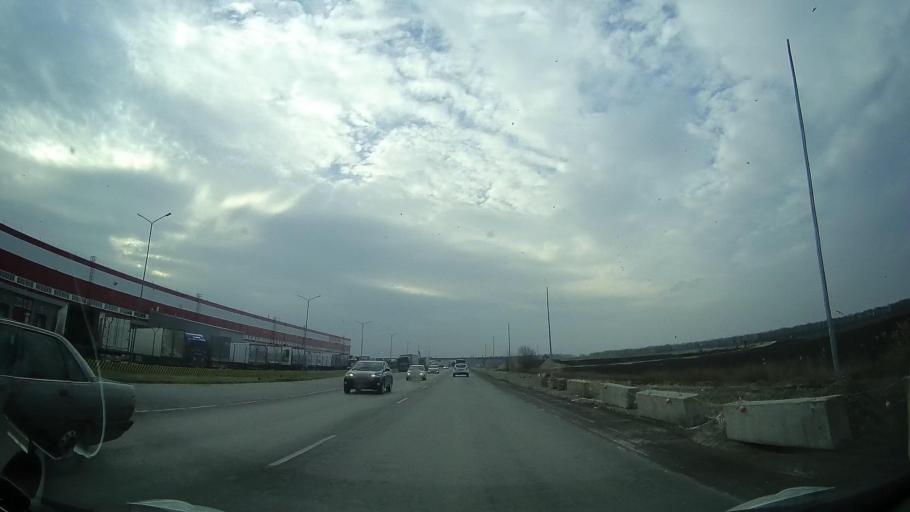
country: RU
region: Rostov
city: Ol'ginskaya
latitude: 47.1299
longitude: 39.9029
